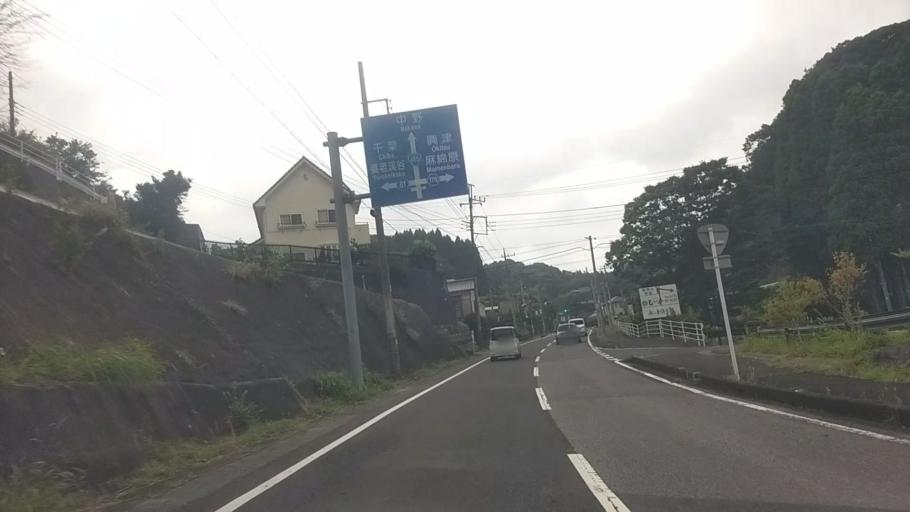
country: JP
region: Chiba
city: Kawaguchi
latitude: 35.2413
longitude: 140.1686
